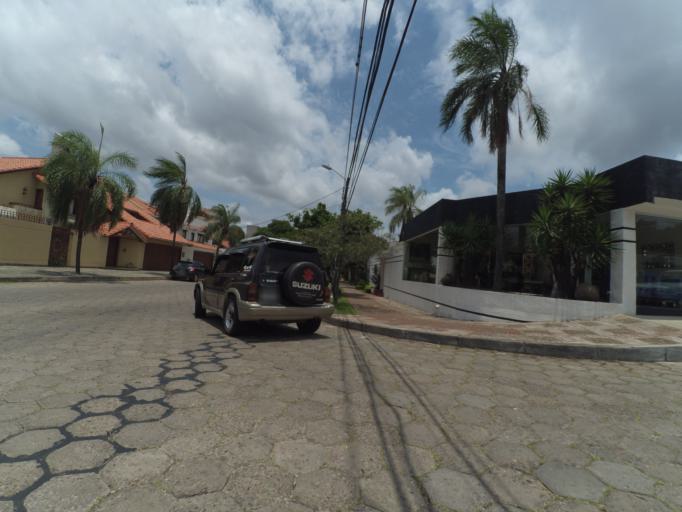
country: BO
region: Santa Cruz
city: Santa Cruz de la Sierra
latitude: -17.7940
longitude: -63.1983
